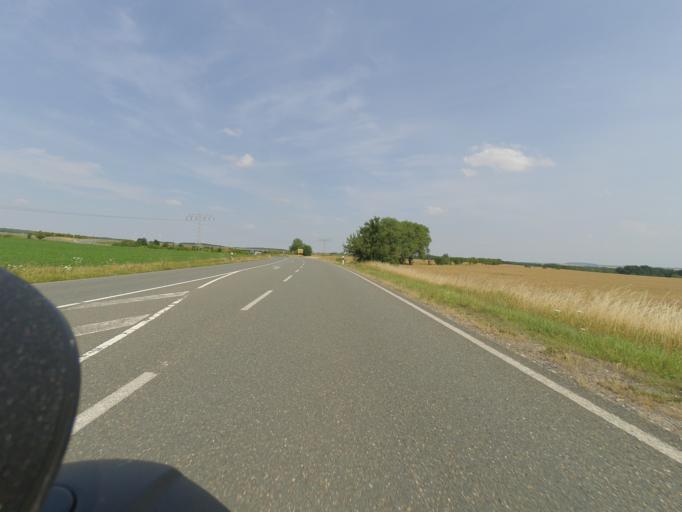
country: DE
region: Thuringia
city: Schwaara
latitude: 50.9376
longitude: 12.1101
